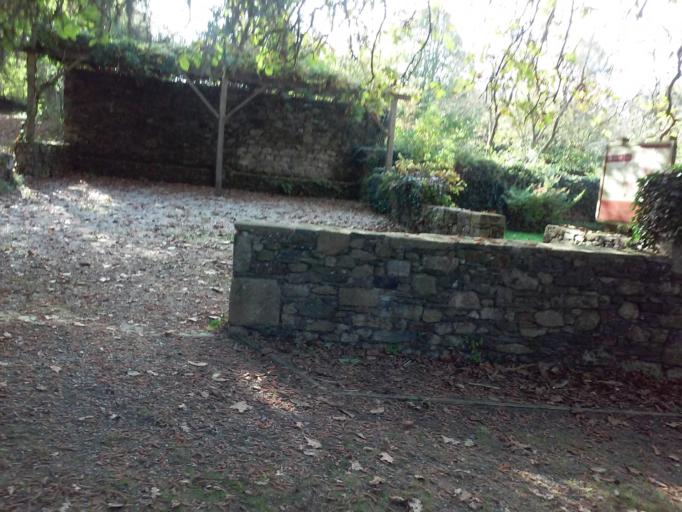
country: FR
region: Pays de la Loire
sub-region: Departement de la Vendee
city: Les Lucs-sur-Boulogne
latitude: 46.8466
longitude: -1.4864
